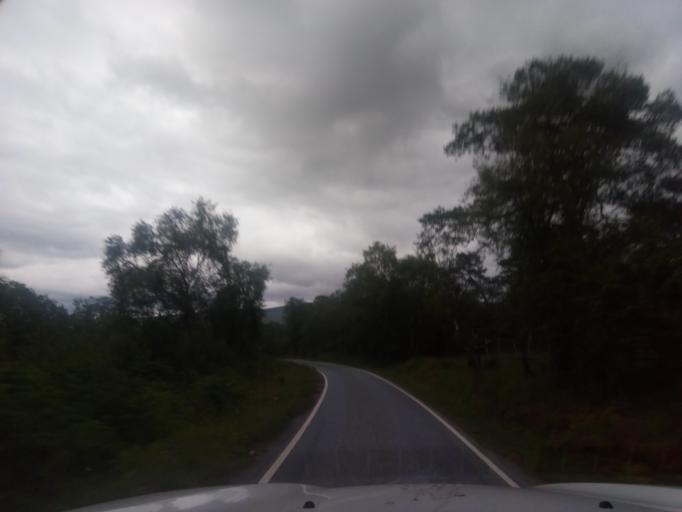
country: GB
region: Scotland
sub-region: Highland
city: Fort William
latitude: 56.8524
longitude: -5.3288
